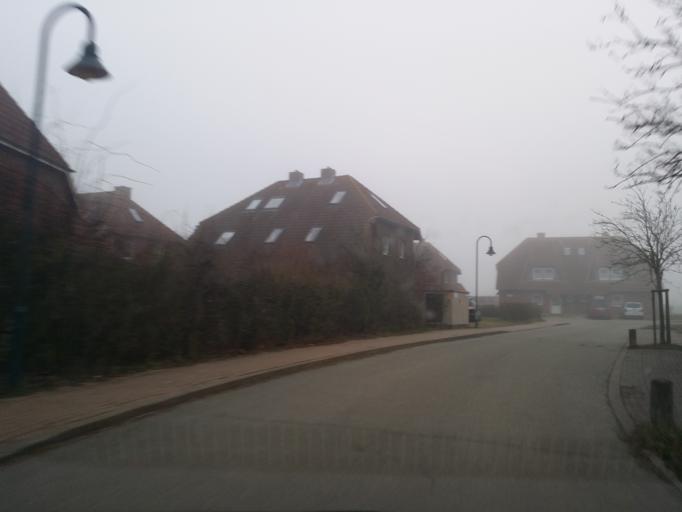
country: DE
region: Schleswig-Holstein
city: Grossenbrode
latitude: 54.4805
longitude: 11.0756
